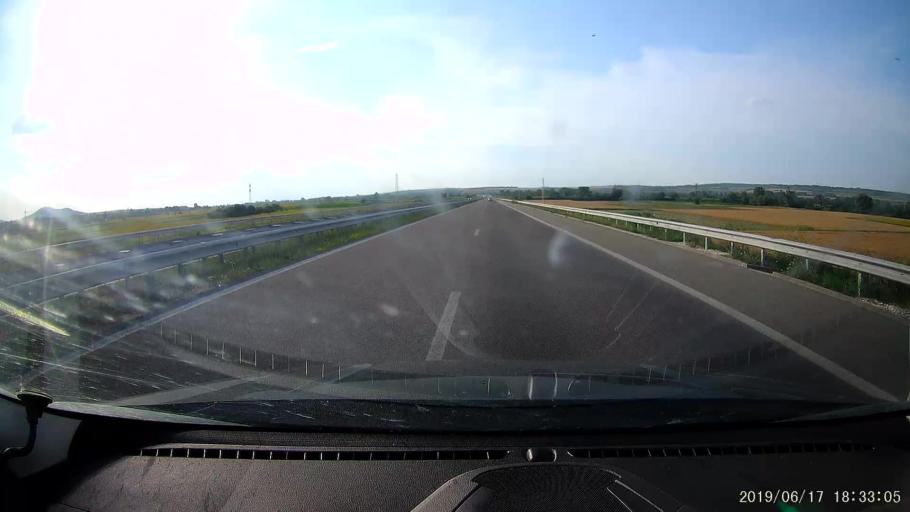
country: BG
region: Khaskovo
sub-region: Obshtina Dimitrovgrad
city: Dimitrovgrad
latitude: 42.0721
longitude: 25.4655
